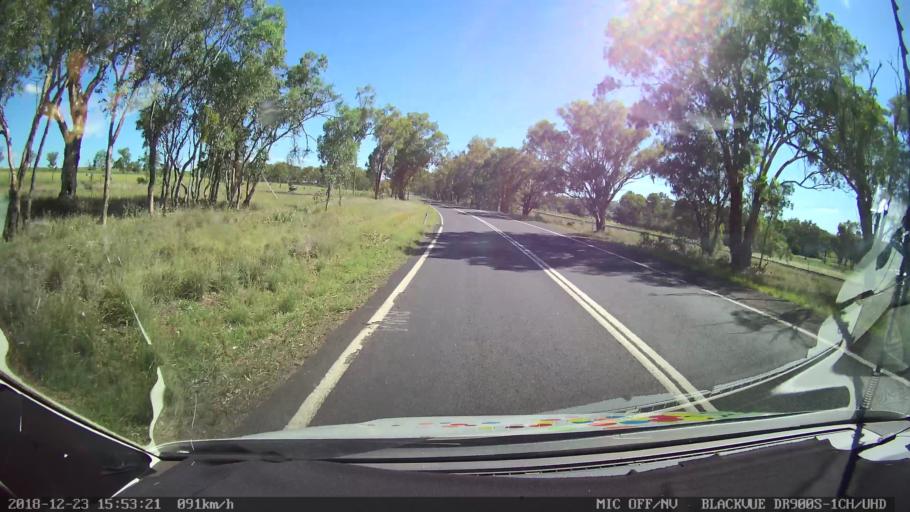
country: AU
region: New South Wales
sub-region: Tamworth Municipality
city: Phillip
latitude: -31.1320
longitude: 150.8816
